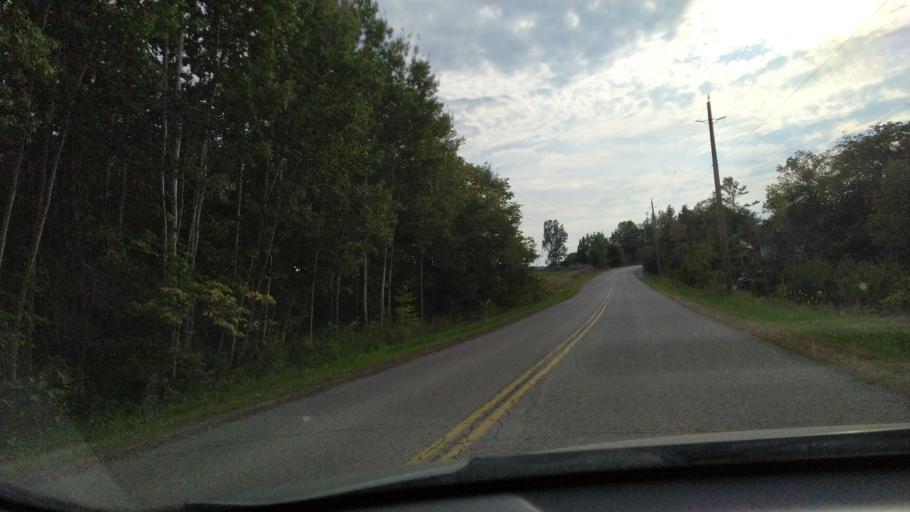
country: CA
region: Ontario
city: Stratford
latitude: 43.4640
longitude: -80.7718
